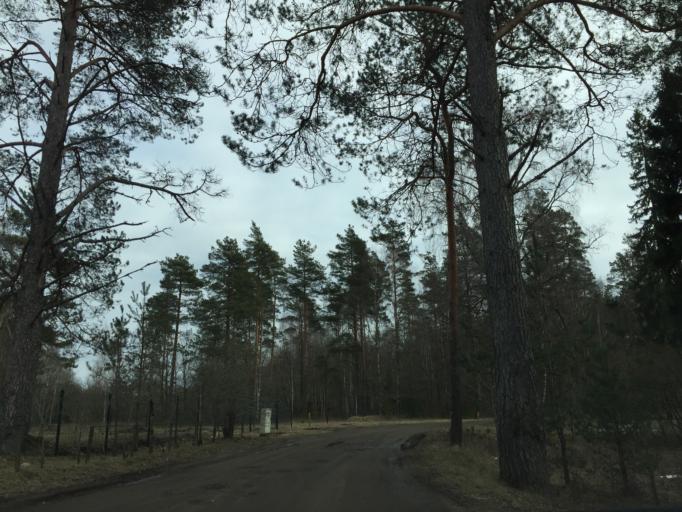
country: LV
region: Garkalne
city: Garkalne
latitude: 57.0742
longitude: 24.4360
